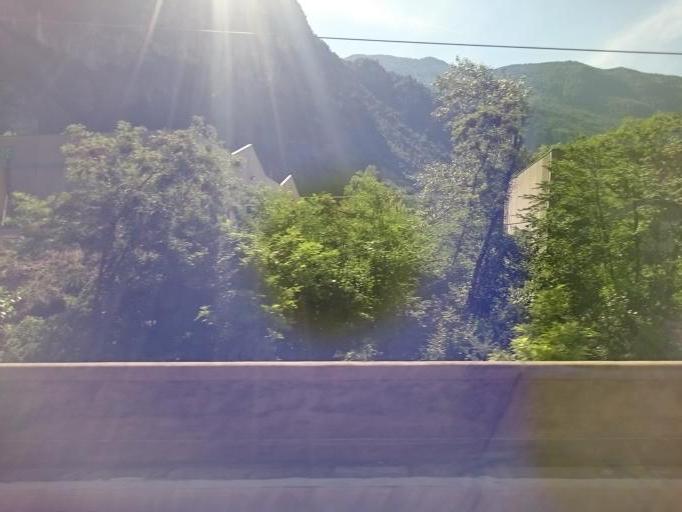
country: IT
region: Trentino-Alto Adige
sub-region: Provincia di Trento
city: Besenello
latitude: 45.9524
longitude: 11.1075
